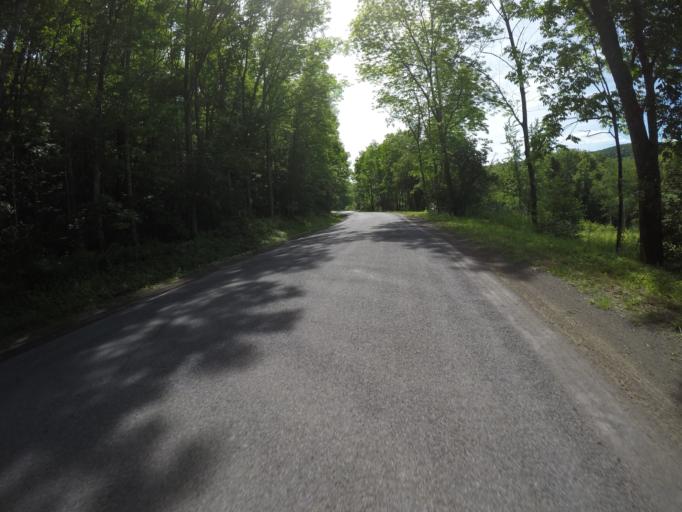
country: US
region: New York
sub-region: Delaware County
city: Stamford
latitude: 42.1323
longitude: -74.6601
